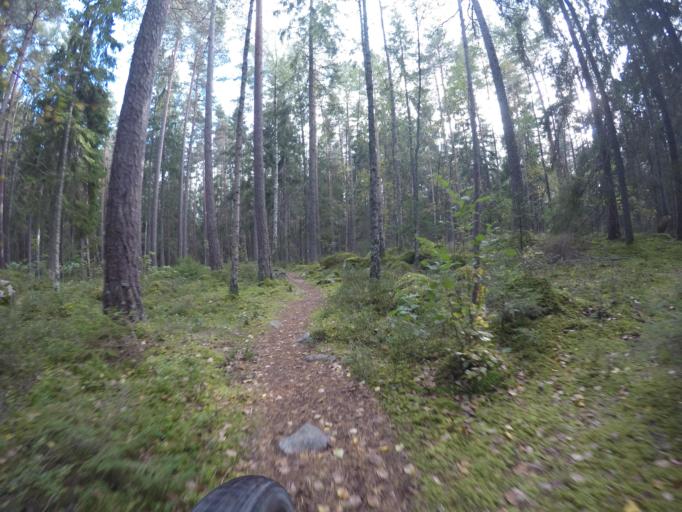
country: SE
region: Vaestmanland
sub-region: Kopings Kommun
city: Koping
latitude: 59.5306
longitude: 16.0008
